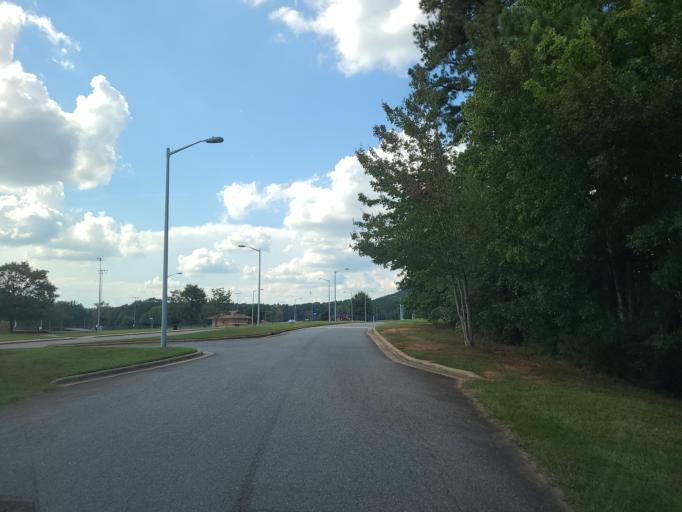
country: US
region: North Carolina
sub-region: Gaston County
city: Lowell
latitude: 35.2870
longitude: -81.1100
